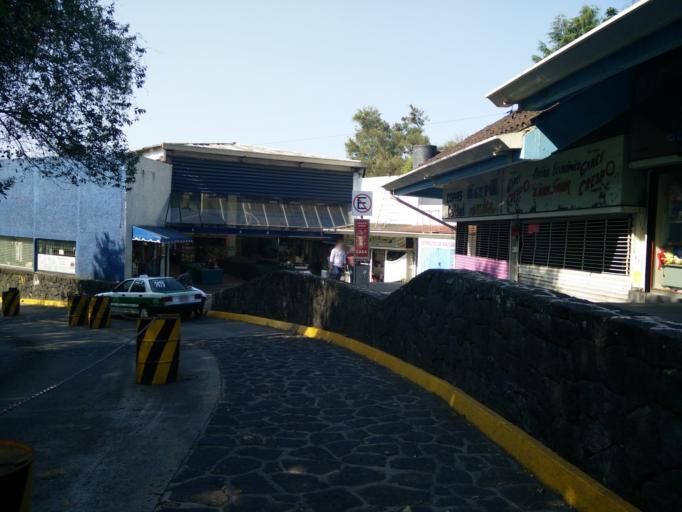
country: MX
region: Veracruz
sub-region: Xalapa
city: Xalapa de Enriquez
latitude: 19.5263
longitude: -96.9039
